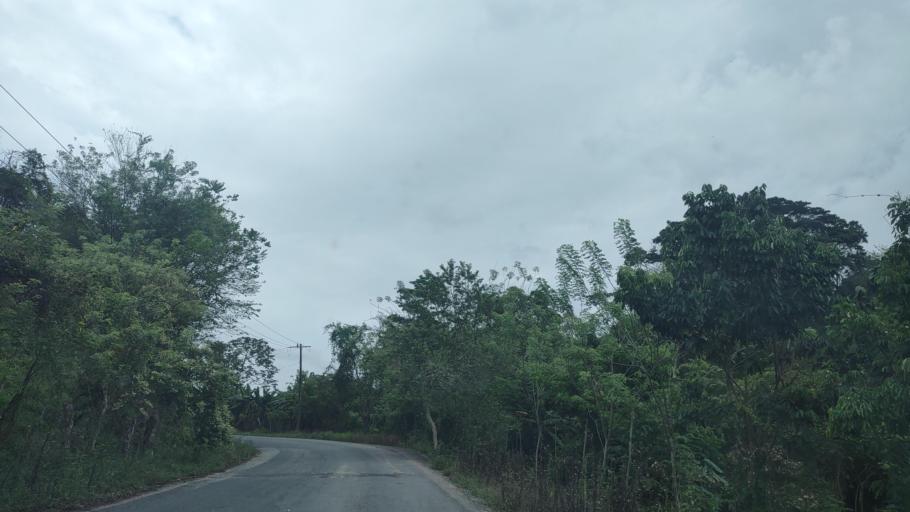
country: MX
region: Tabasco
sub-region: Huimanguillo
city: Francisco Rueda
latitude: 17.5242
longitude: -94.1256
